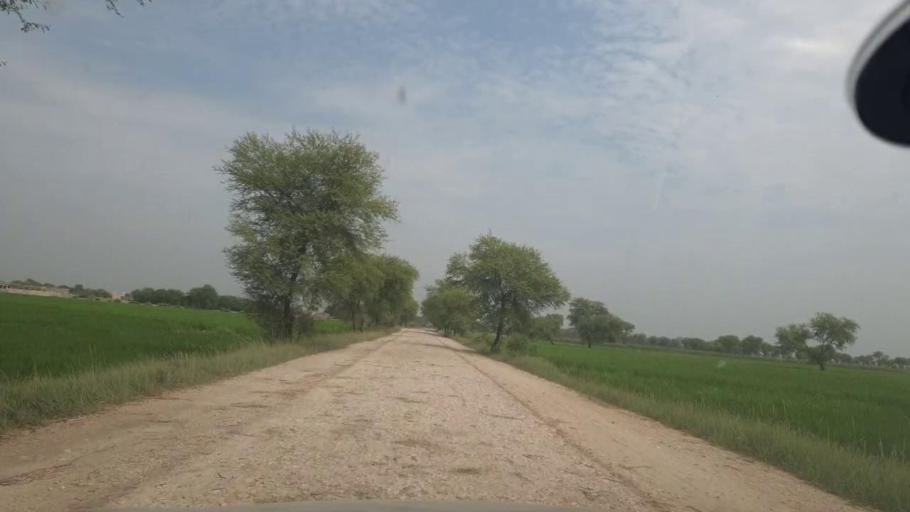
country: PK
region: Sindh
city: Jacobabad
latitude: 28.2491
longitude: 68.5424
